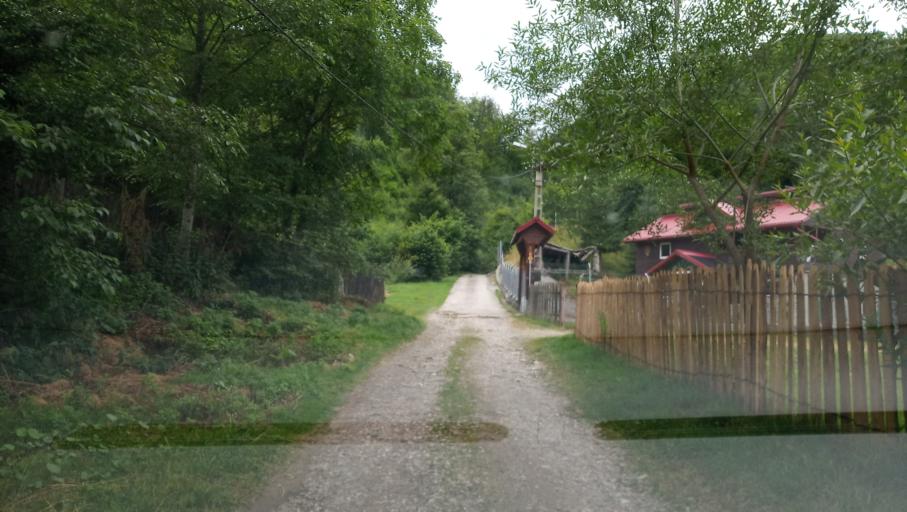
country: RO
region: Hunedoara
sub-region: Oras Petrila
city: Petrila
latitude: 45.4887
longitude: 23.4186
